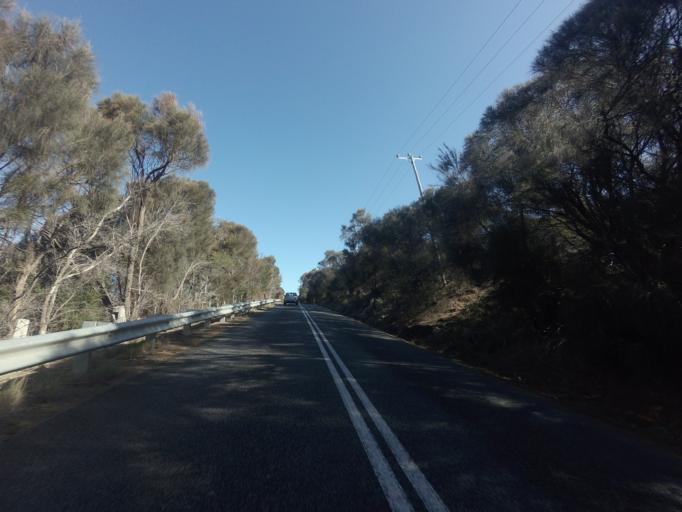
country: AU
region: Tasmania
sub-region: Sorell
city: Sorell
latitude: -42.2200
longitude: 148.0298
